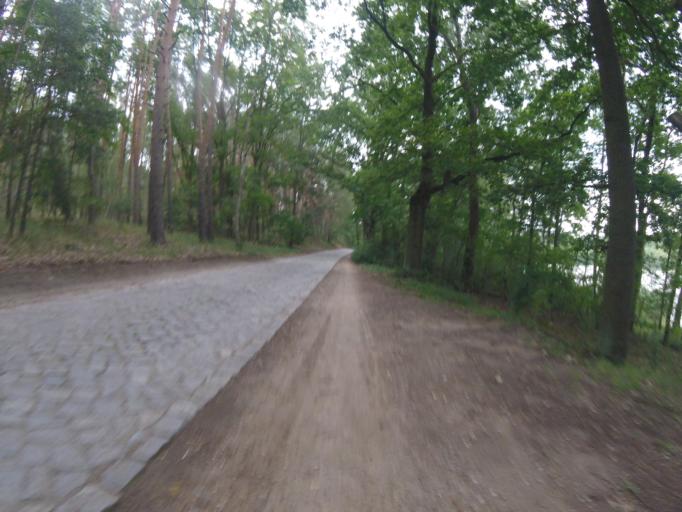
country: DE
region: Brandenburg
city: Schwerin
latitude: 52.1873
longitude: 13.5936
